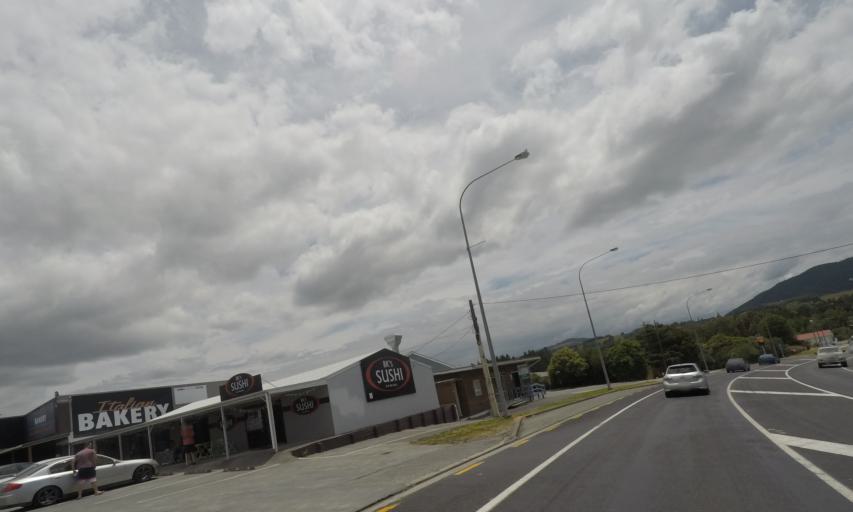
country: NZ
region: Auckland
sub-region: Auckland
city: Wellsford
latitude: -36.1647
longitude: 174.4433
